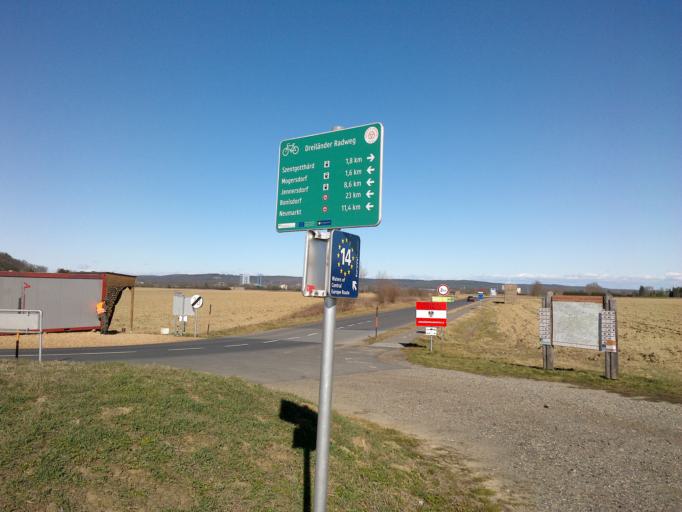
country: AT
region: Burgenland
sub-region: Politischer Bezirk Jennersdorf
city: Mogersdorf
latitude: 46.9521
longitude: 16.2449
